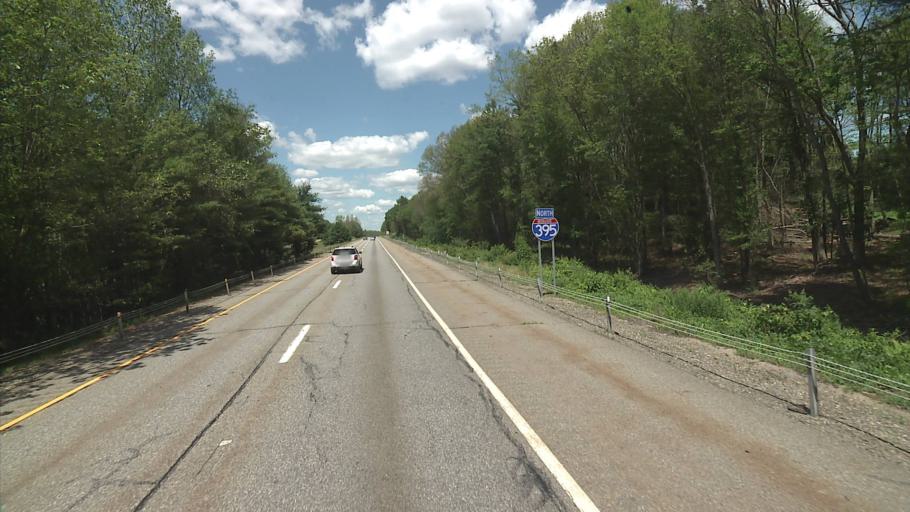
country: US
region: Massachusetts
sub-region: Worcester County
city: Webster
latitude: 42.0156
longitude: -71.8574
